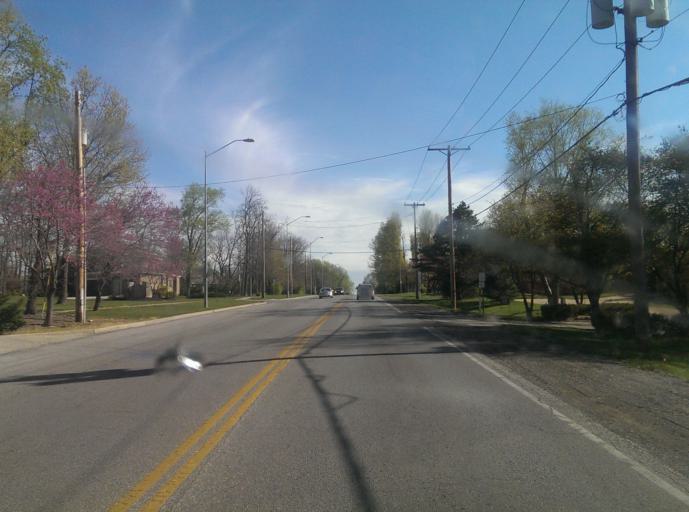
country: US
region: Missouri
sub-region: Jackson County
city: Grandview
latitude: 38.9012
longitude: -94.5944
